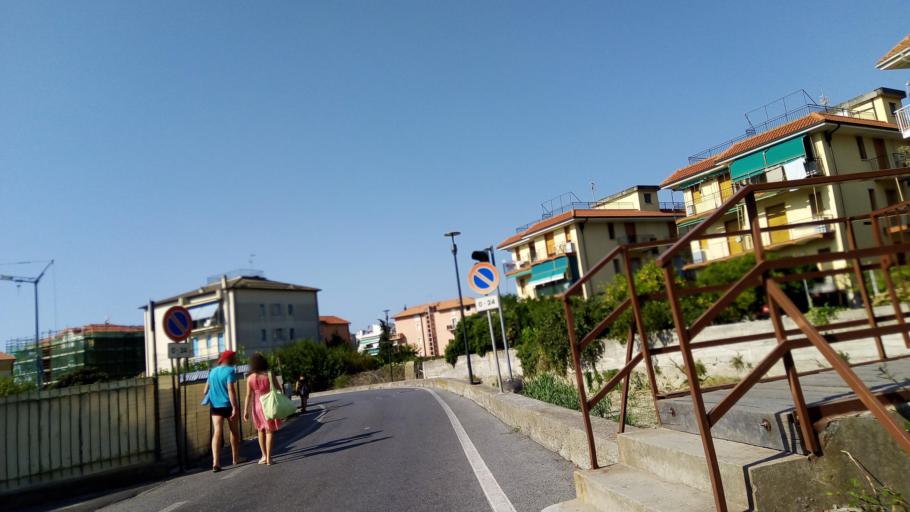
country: IT
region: Liguria
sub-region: Provincia di Savona
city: Borgio
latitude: 44.1585
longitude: 8.3022
